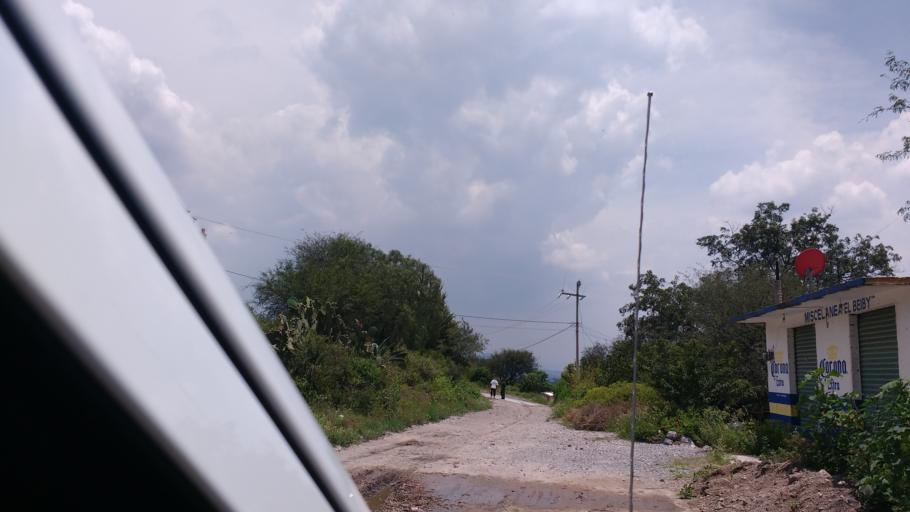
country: MX
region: Hidalgo
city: Mixquiahuala de Juarez
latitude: 20.2507
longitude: -99.2417
